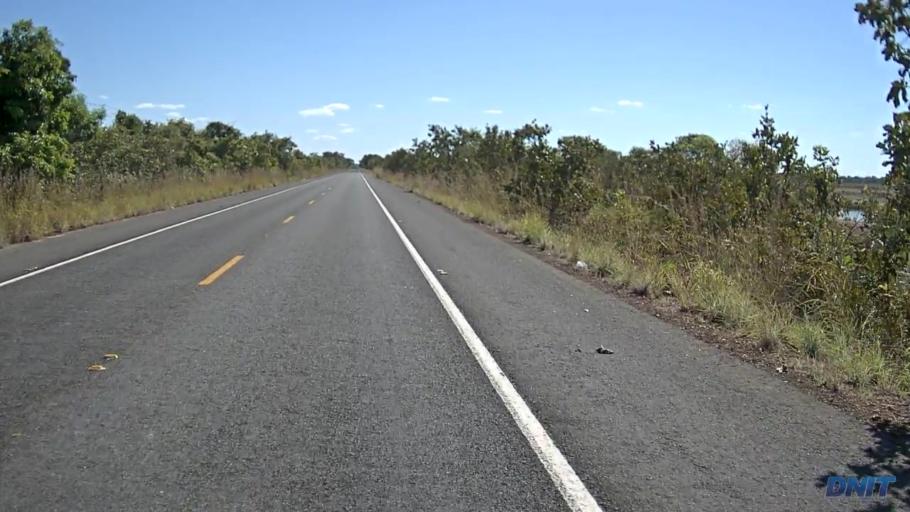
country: BR
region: Goias
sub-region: Sao Miguel Do Araguaia
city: Sao Miguel do Araguaia
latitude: -13.2381
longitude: -50.5483
